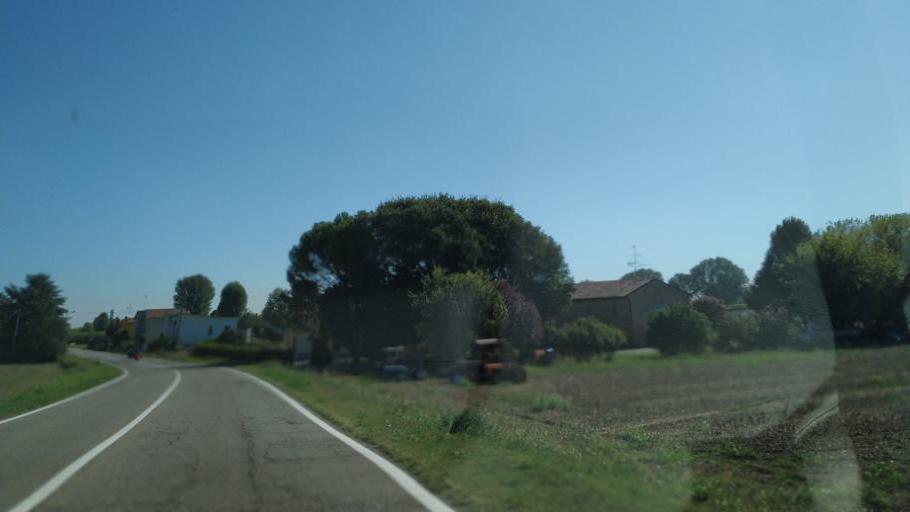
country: IT
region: Emilia-Romagna
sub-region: Provincia di Ferrara
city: Sant'Agostino
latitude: 44.7938
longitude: 11.3964
